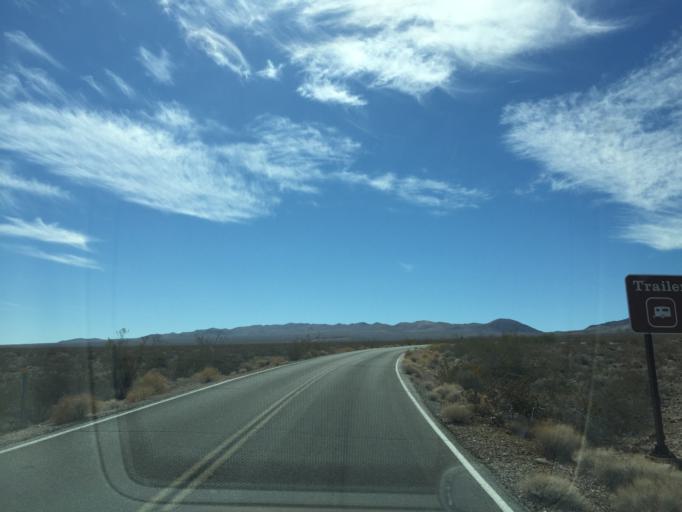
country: US
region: Nevada
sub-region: Nye County
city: Beatty
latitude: 36.2706
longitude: -116.6632
